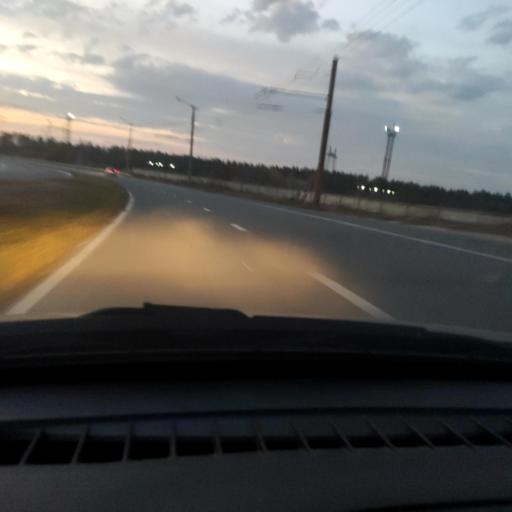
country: RU
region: Samara
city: Povolzhskiy
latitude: 53.5478
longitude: 49.6008
